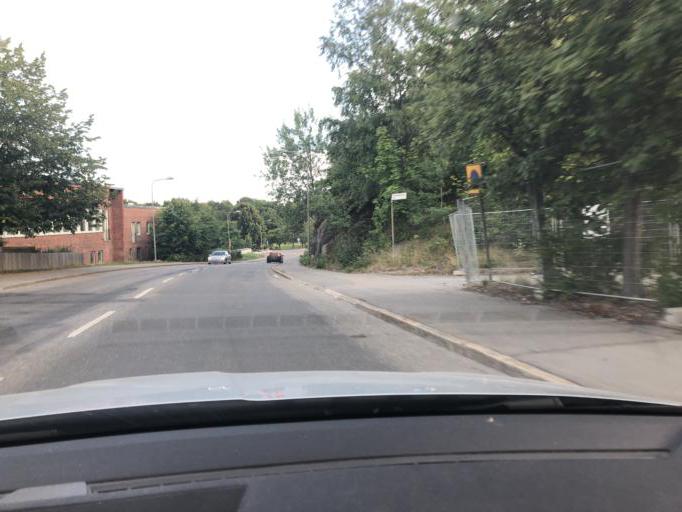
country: SE
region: Stockholm
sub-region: Botkyrka Kommun
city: Fittja
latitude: 59.2739
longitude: 17.8867
